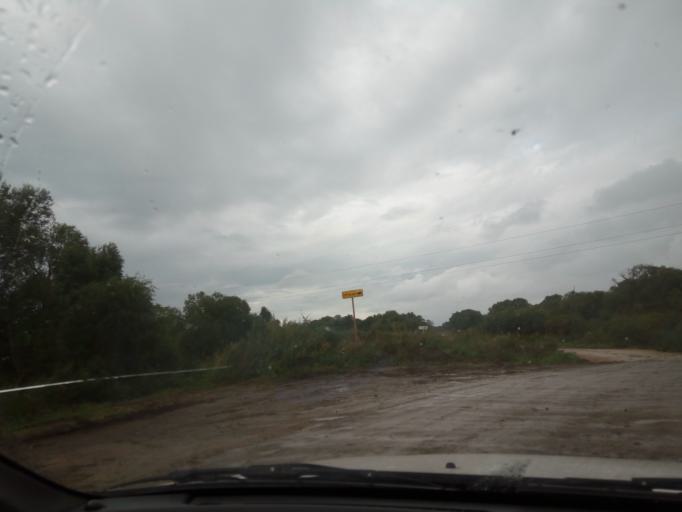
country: RU
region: Primorskiy
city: Lazo
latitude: 45.8526
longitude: 133.6462
